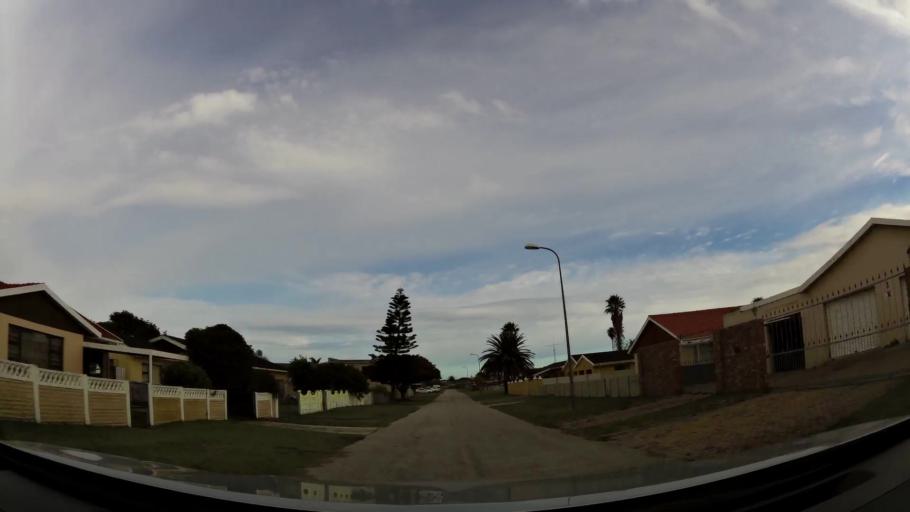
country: ZA
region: Eastern Cape
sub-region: Nelson Mandela Bay Metropolitan Municipality
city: Port Elizabeth
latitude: -33.9365
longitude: 25.4663
